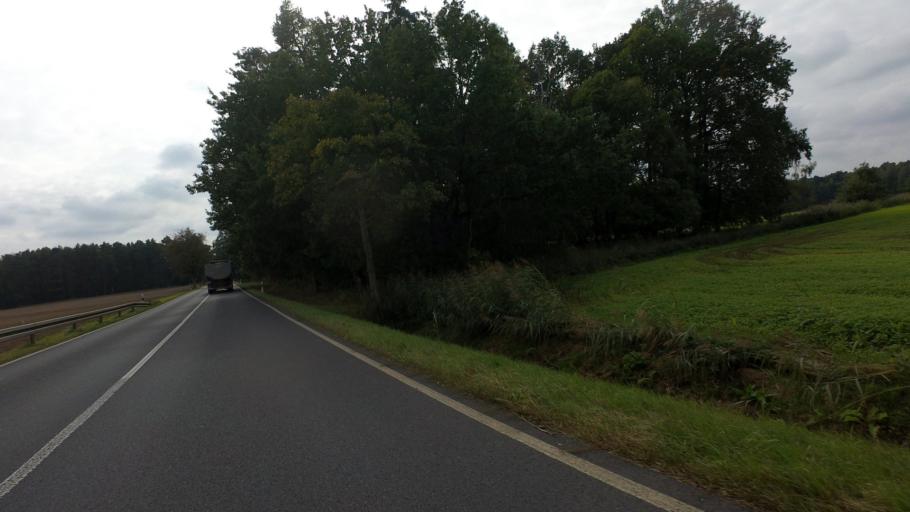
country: DE
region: Brandenburg
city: Kasel-Golzig
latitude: 51.8944
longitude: 13.6843
